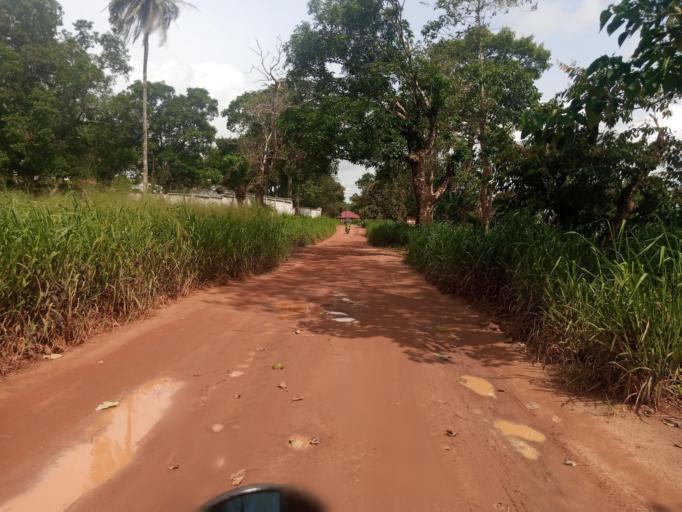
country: SL
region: Southern Province
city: Bo
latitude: 7.9688
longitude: -11.7531
